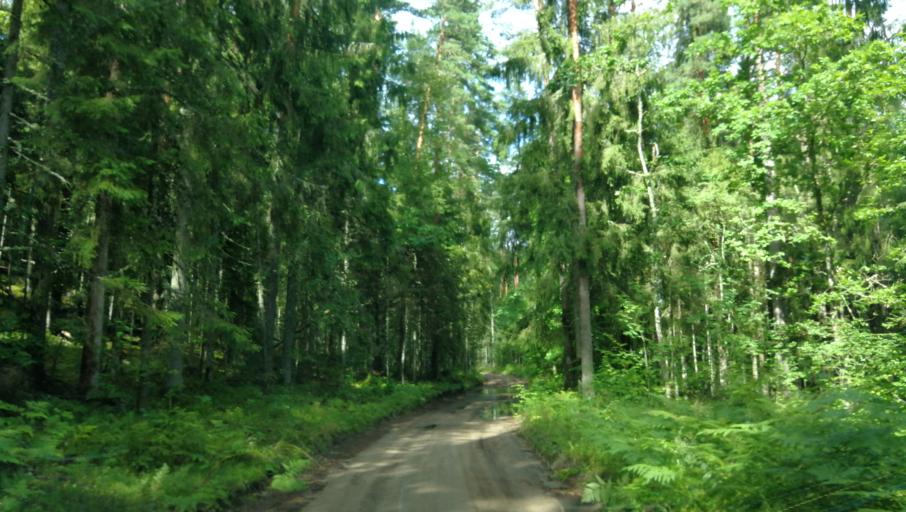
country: LV
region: Cesu Rajons
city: Cesis
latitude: 57.3062
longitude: 25.2127
